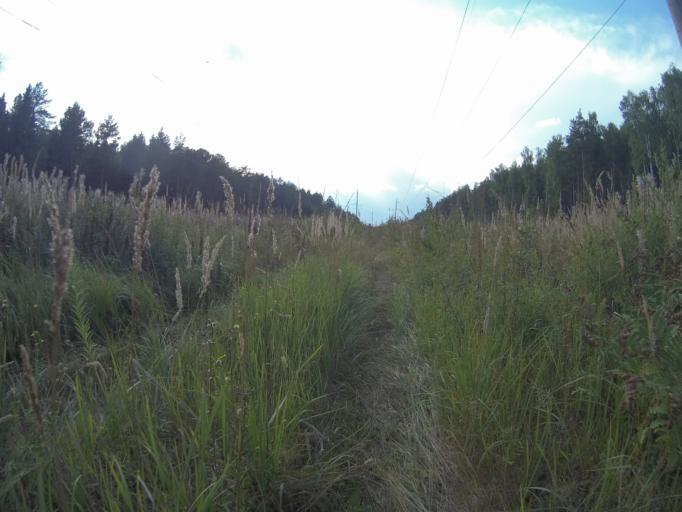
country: RU
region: Vladimir
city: Raduzhnyy
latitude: 56.0135
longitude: 40.2840
